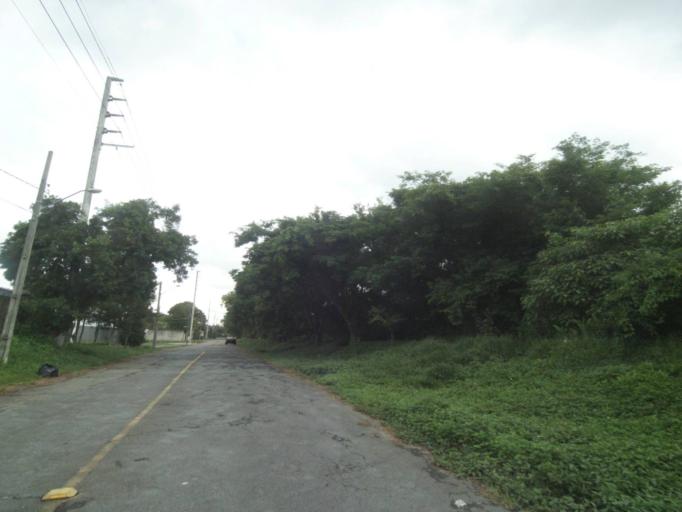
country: BR
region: Parana
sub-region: Curitiba
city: Curitiba
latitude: -25.4434
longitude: -49.3162
